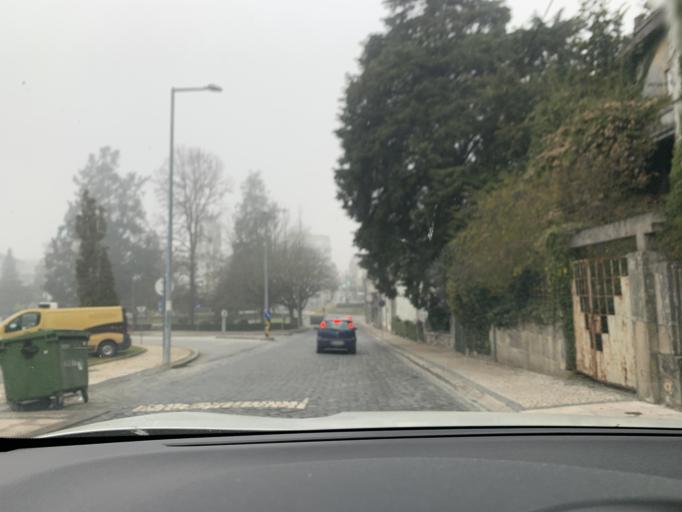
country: PT
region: Viseu
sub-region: Viseu
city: Viseu
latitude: 40.6569
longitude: -7.9086
